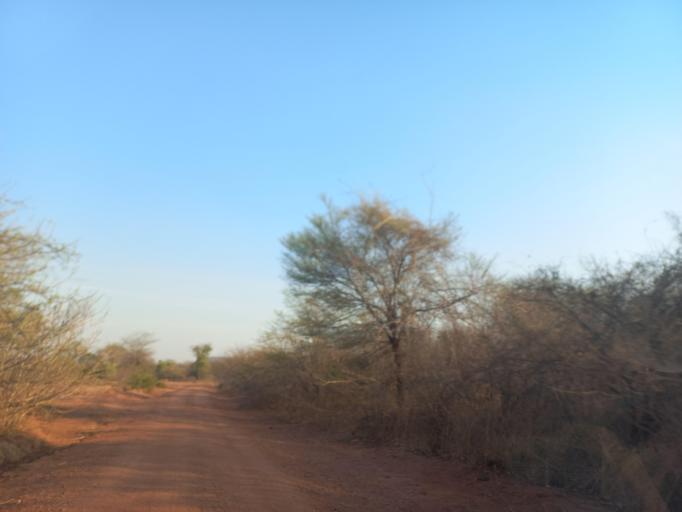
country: ZM
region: Lusaka
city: Luangwa
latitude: -15.4472
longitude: 30.3715
